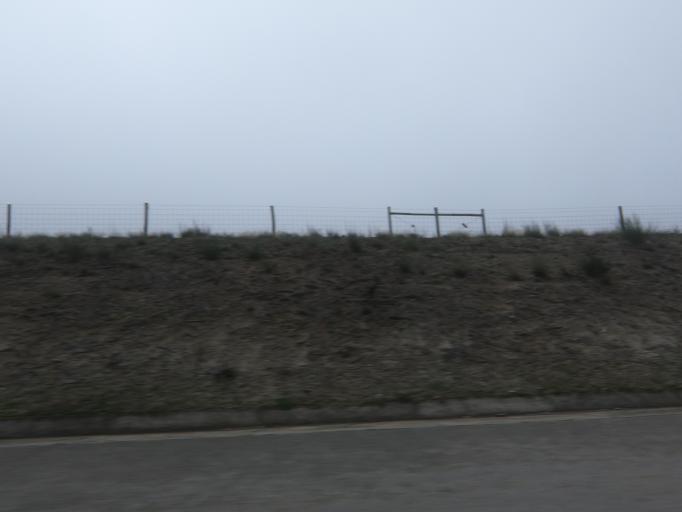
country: PT
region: Viseu
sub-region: Tarouca
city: Tarouca
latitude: 41.0265
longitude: -7.8717
